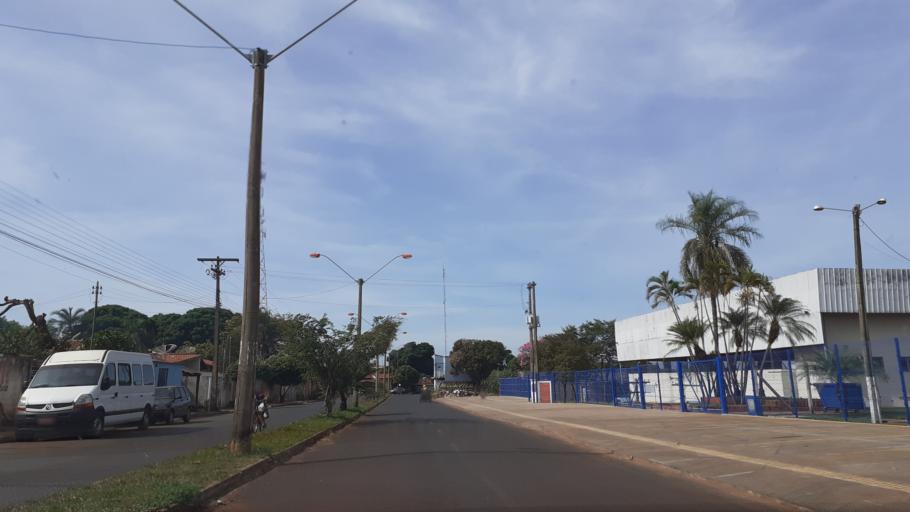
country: BR
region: Goias
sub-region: Itumbiara
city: Itumbiara
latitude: -18.4178
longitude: -49.2336
